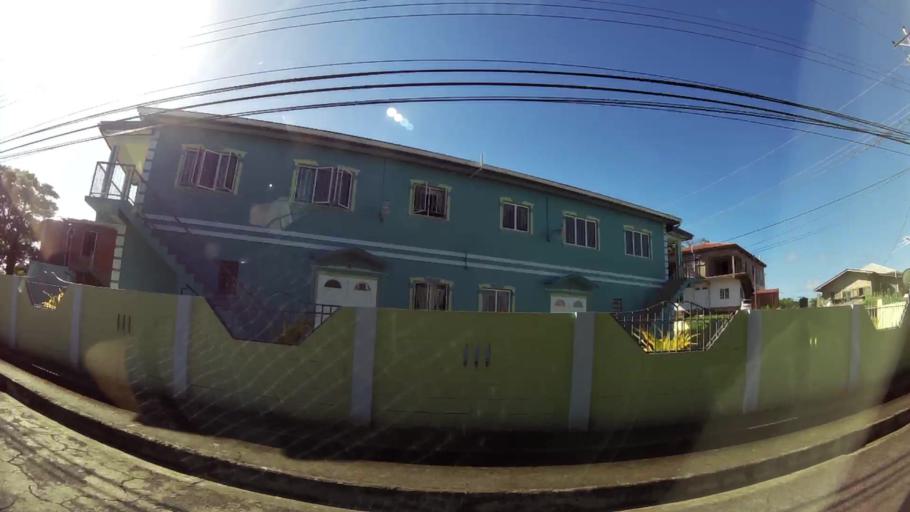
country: TT
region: Tobago
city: Scarborough
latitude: 11.1590
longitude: -60.8253
